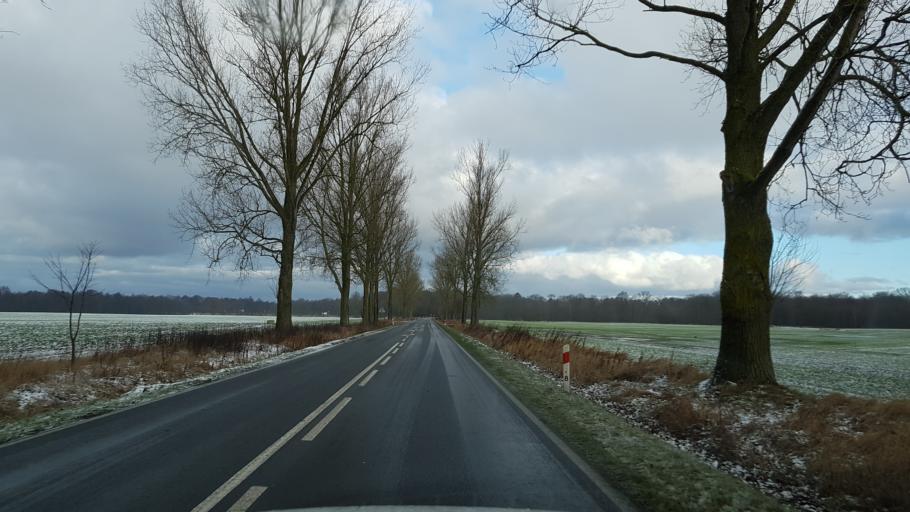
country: PL
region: West Pomeranian Voivodeship
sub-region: Powiat gryficki
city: Karnice
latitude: 54.0209
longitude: 15.0612
